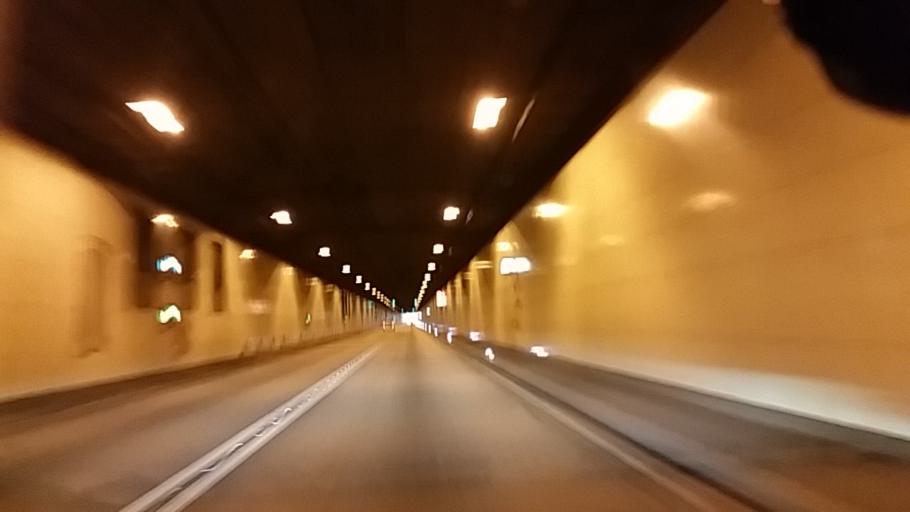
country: DE
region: Hamburg
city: Altona
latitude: 53.5400
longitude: 9.9216
